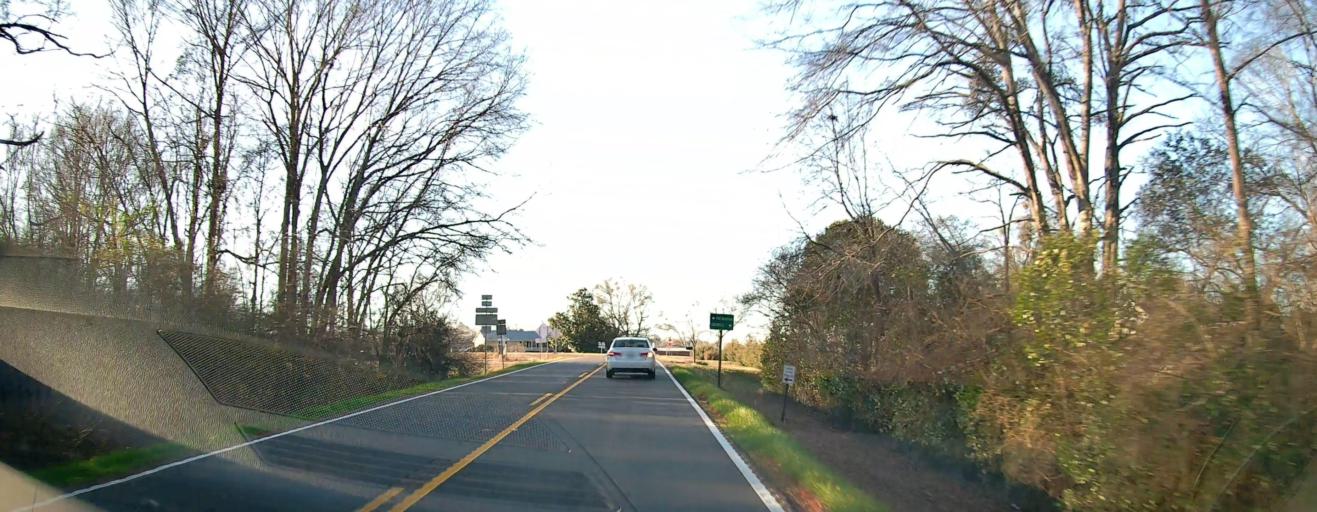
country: US
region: Georgia
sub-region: Harris County
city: Pine Mountain
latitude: 32.9212
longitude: -84.7677
